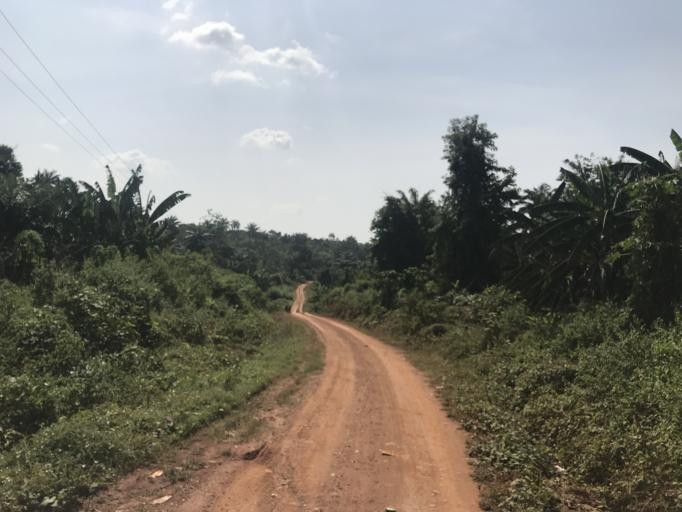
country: NG
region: Osun
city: Osu
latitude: 7.6352
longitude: 4.6708
